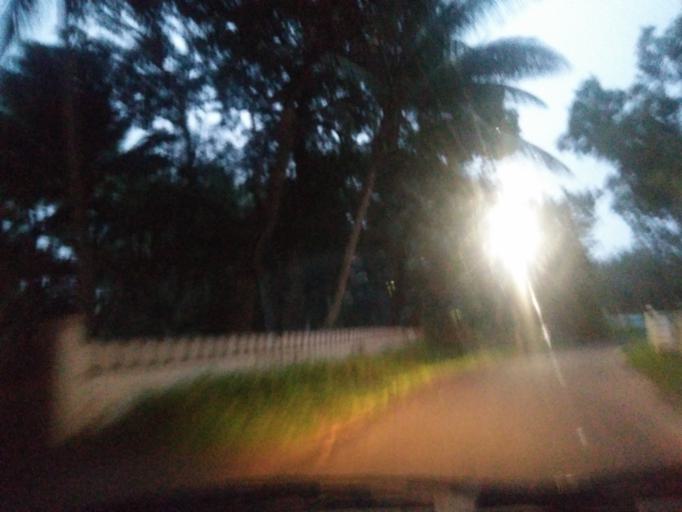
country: IN
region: Goa
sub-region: South Goa
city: Varca
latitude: 15.2221
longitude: 73.9553
